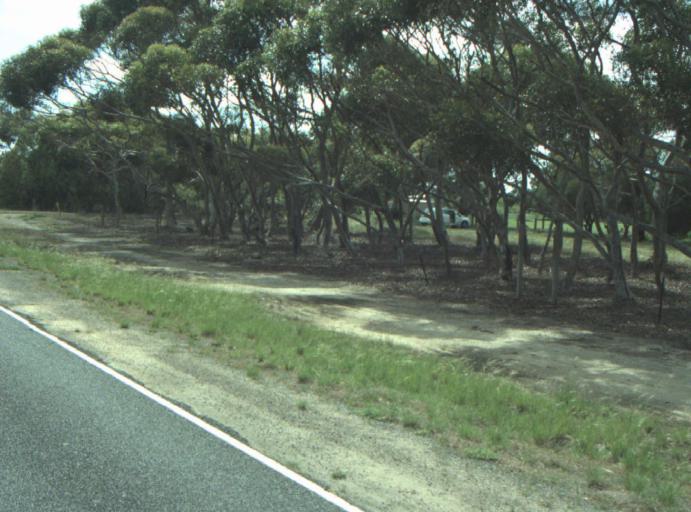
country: AU
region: Victoria
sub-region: Wyndham
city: Little River
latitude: -37.9844
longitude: 144.4976
